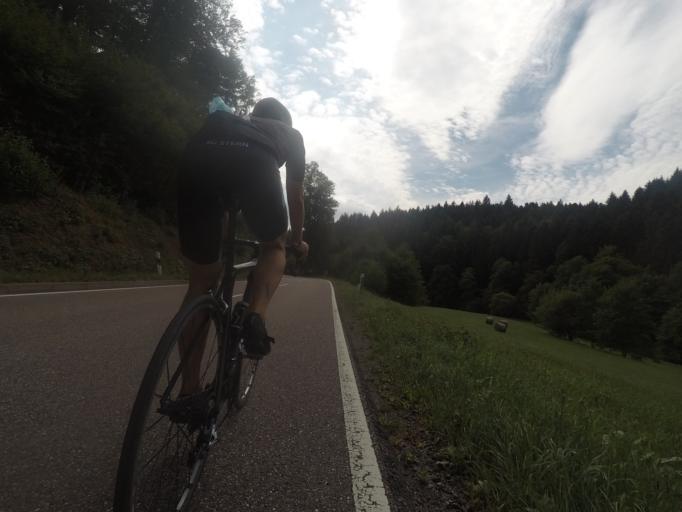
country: DE
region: Baden-Wuerttemberg
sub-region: Karlsruhe Region
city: Bad Herrenalb
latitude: 48.8520
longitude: 8.4586
